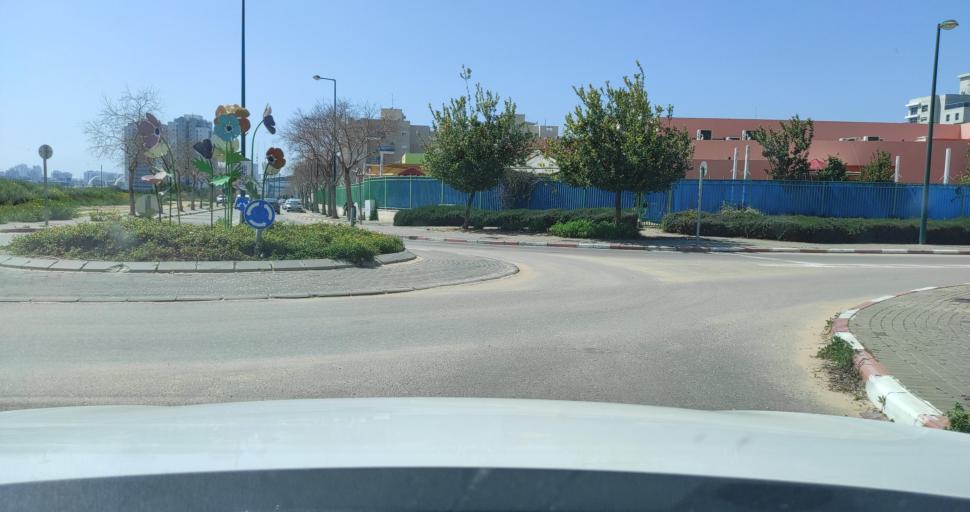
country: IL
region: Central District
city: Nordiyya
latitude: 32.2956
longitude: 34.8757
